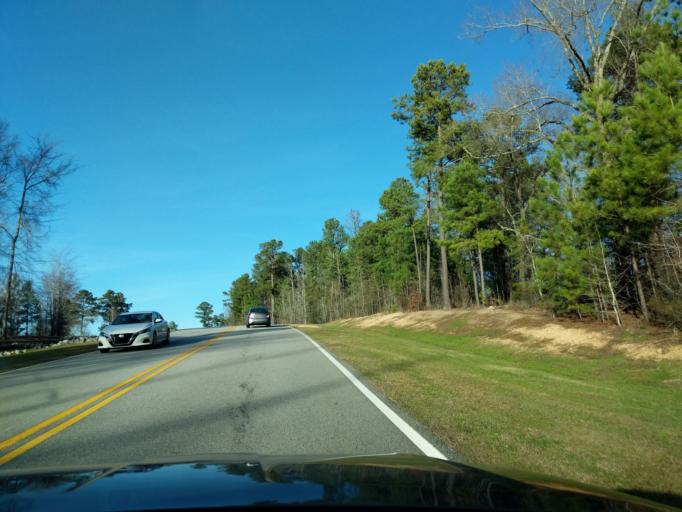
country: US
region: Georgia
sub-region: Columbia County
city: Evans
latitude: 33.5837
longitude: -82.1997
